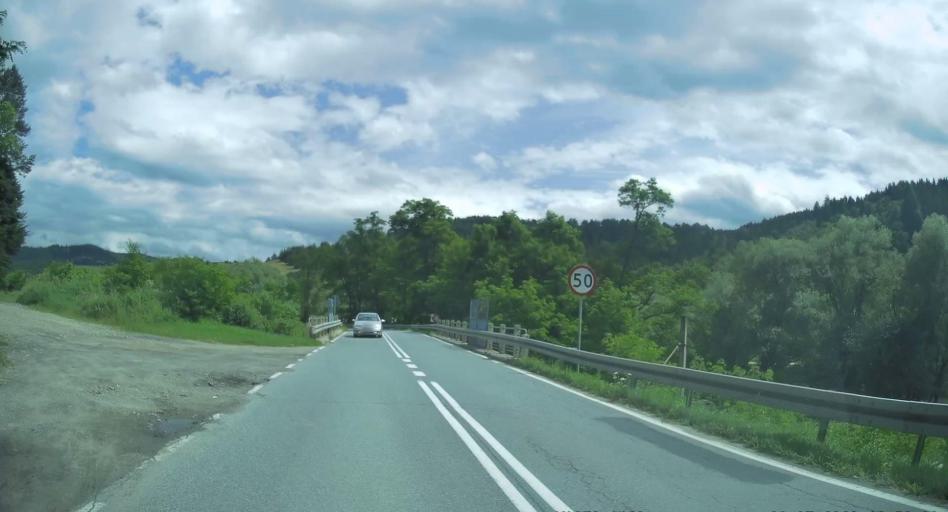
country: PL
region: Lesser Poland Voivodeship
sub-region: Powiat nowosadecki
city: Piwniczna-Zdroj
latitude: 49.3719
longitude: 20.7641
